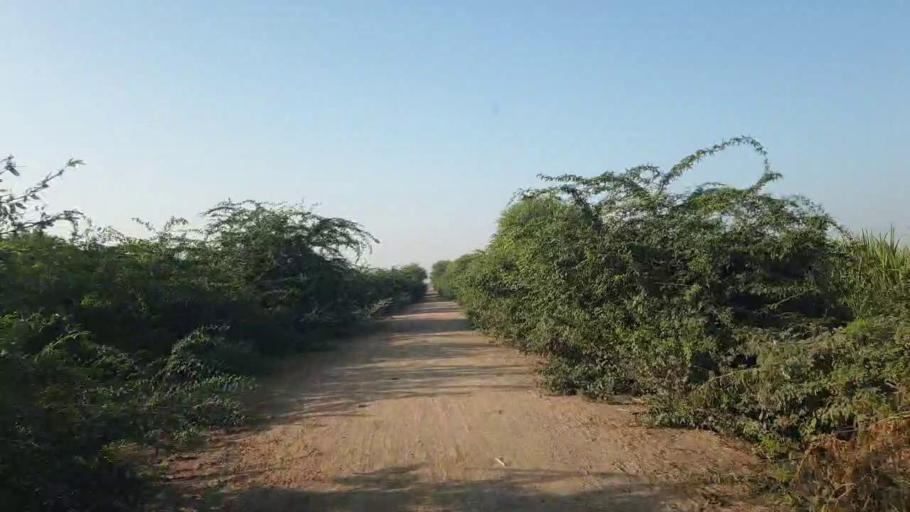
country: PK
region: Sindh
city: Badin
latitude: 24.6016
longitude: 68.7769
